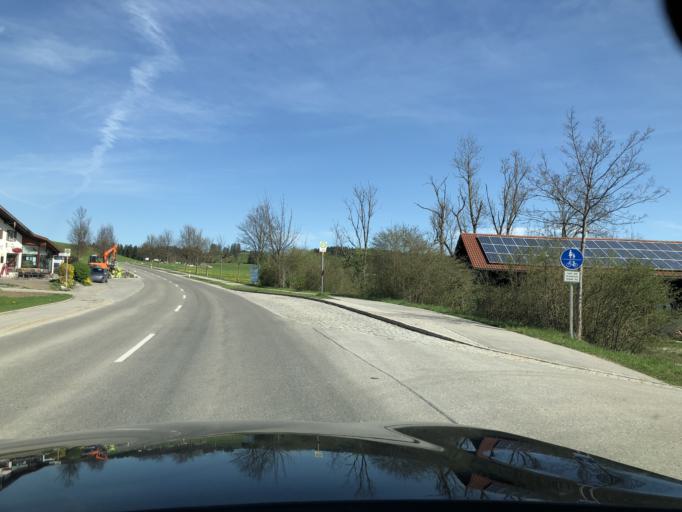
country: DE
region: Bavaria
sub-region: Swabia
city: Eisenberg
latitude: 47.6194
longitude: 10.6090
